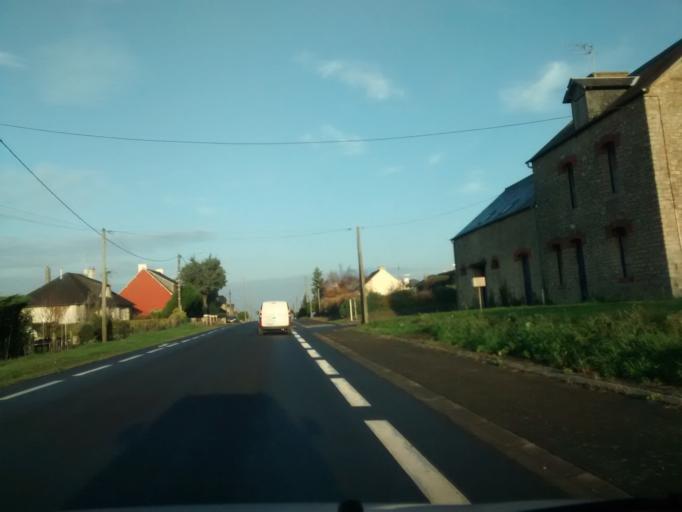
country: FR
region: Lower Normandy
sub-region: Departement de la Manche
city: Pontorson
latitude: 48.5444
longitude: -1.4991
